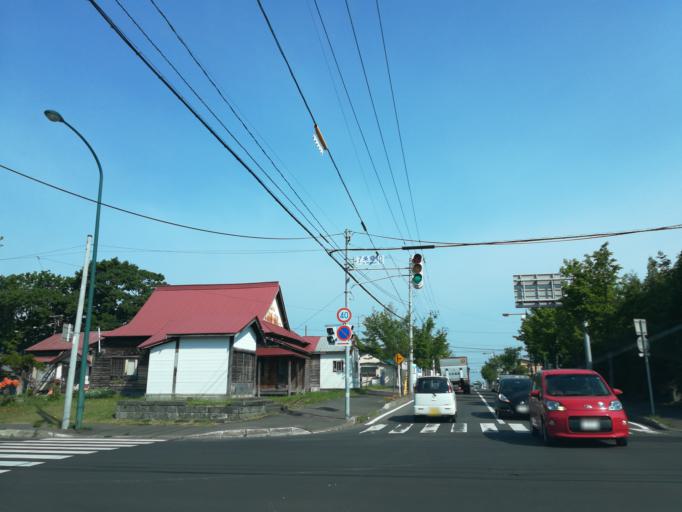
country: JP
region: Hokkaido
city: Iwamizawa
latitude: 43.2054
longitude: 141.7789
